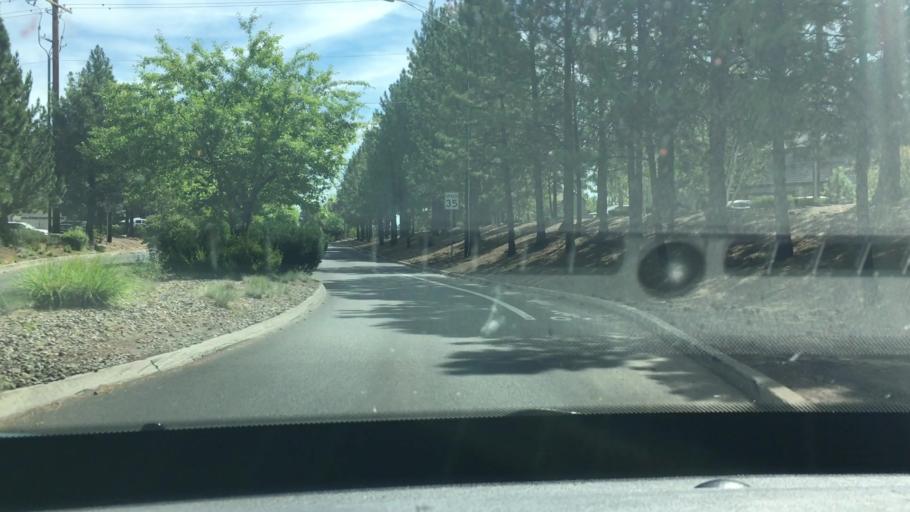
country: US
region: Oregon
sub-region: Deschutes County
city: Bend
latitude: 44.0417
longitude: -121.3317
